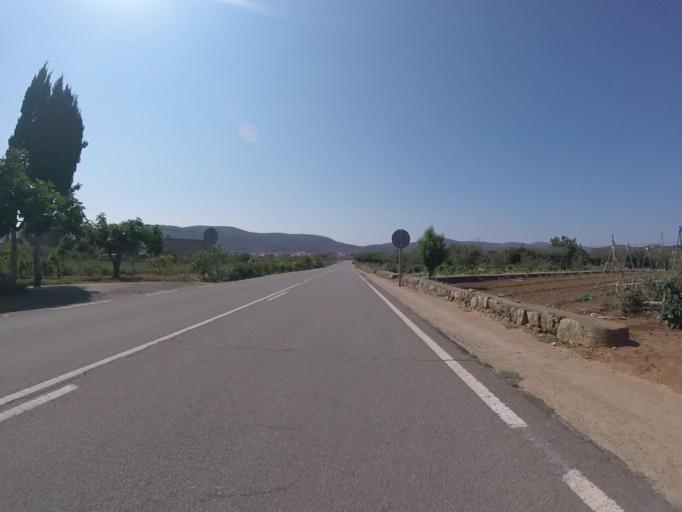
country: ES
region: Valencia
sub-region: Provincia de Castello
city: Adzaneta
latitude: 40.2263
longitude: -0.1733
